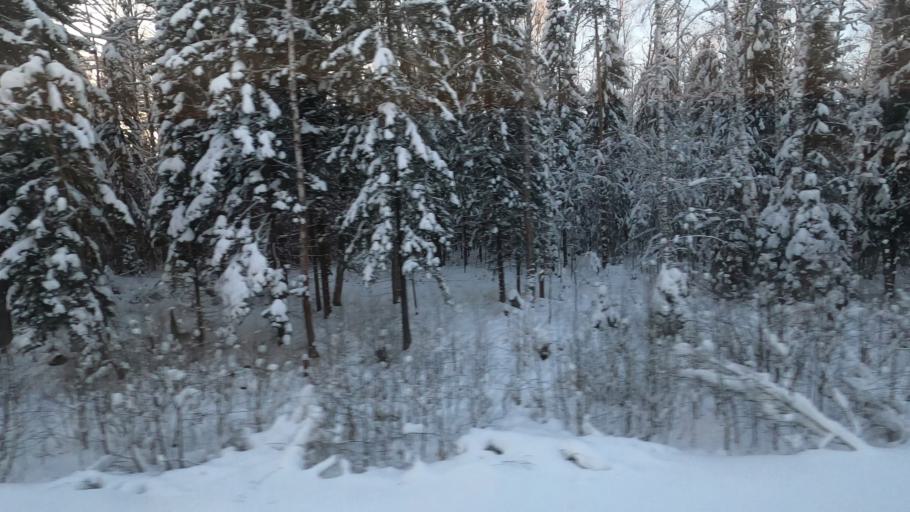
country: RU
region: Moskovskaya
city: Novo-Nikol'skoye
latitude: 56.6011
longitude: 37.5672
